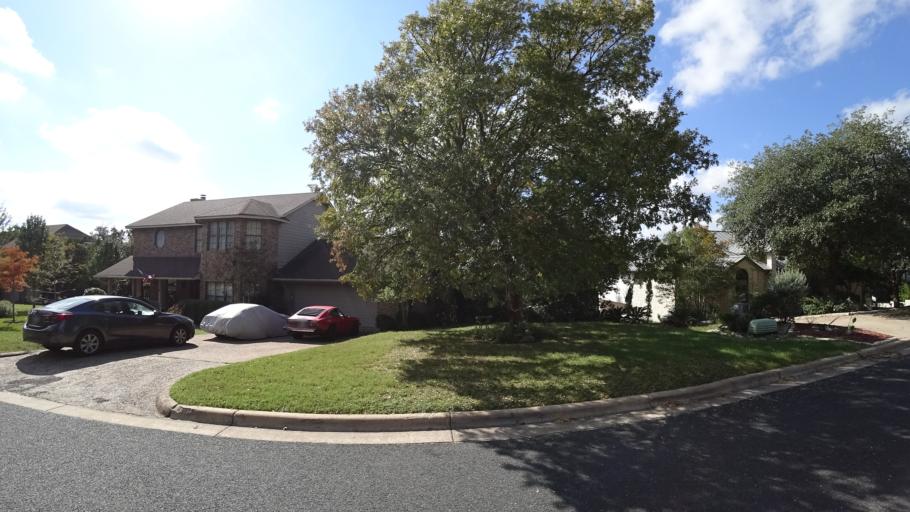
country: US
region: Texas
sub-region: Williamson County
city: Anderson Mill
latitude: 30.4223
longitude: -97.8057
